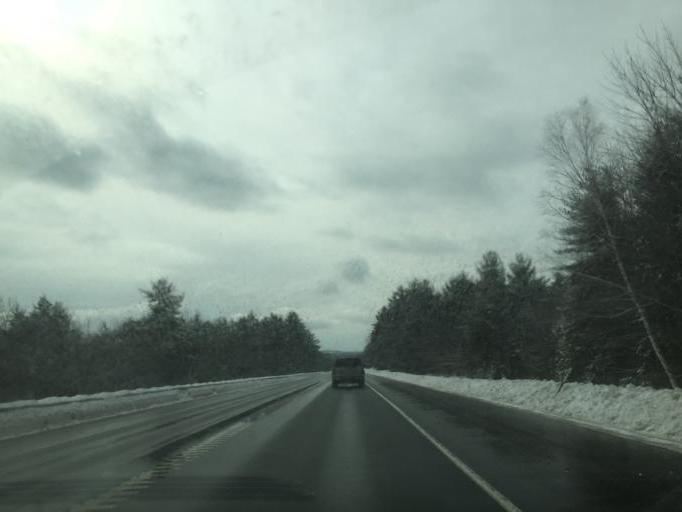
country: US
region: New Hampshire
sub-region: Carroll County
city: Sanbornville
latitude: 43.5139
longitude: -71.0286
